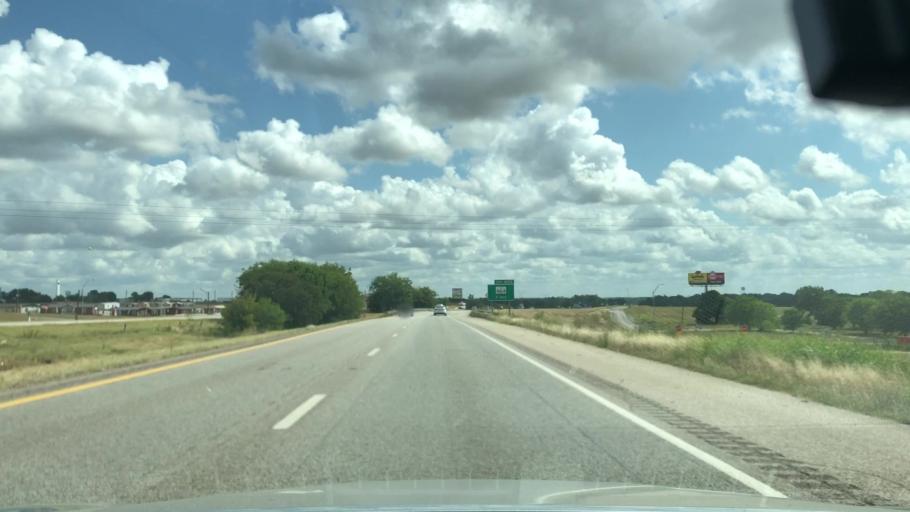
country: US
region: Texas
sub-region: Guadalupe County
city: McQueeney
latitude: 29.5594
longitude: -98.0336
